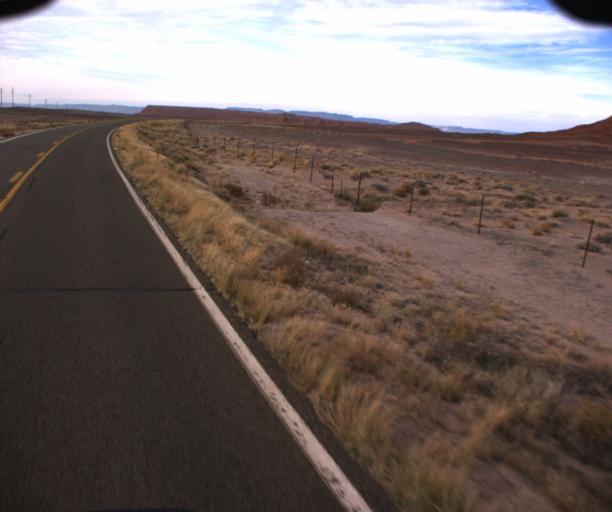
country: US
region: Arizona
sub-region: Apache County
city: Many Farms
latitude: 36.4719
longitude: -109.5211
